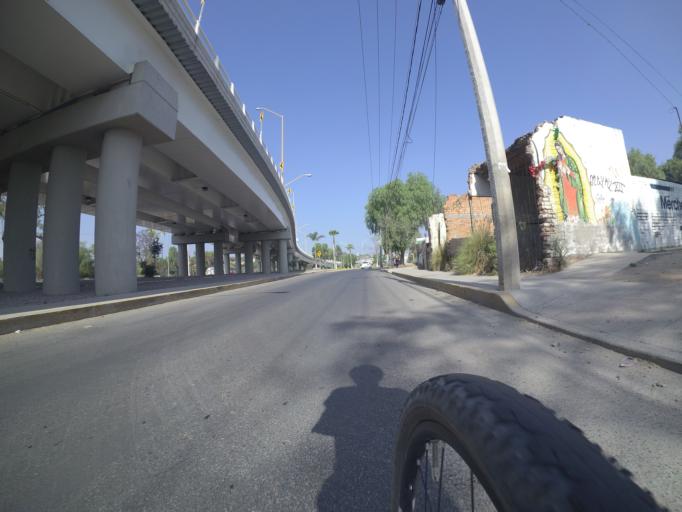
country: MX
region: Aguascalientes
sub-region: Jesus Maria
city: Corral de Barrancos
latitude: 21.9528
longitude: -102.3345
